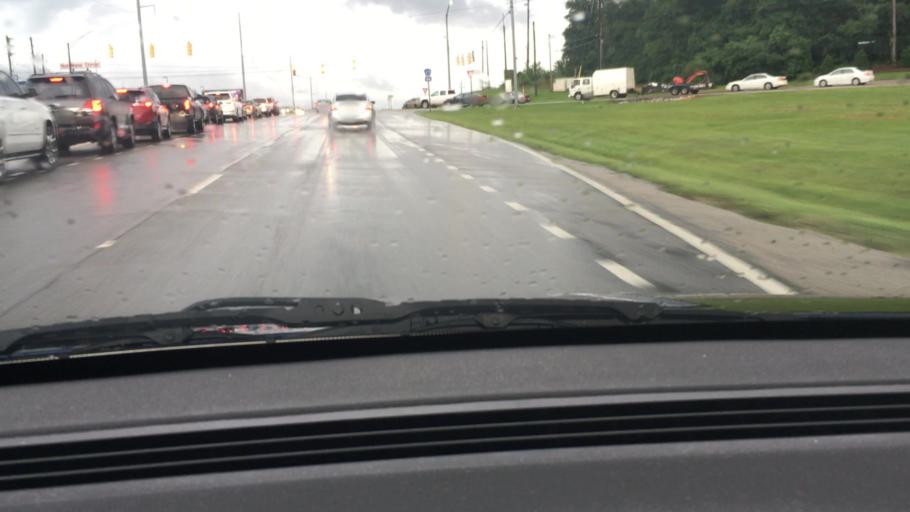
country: US
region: Alabama
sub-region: Tuscaloosa County
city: Northport
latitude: 33.2361
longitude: -87.5532
